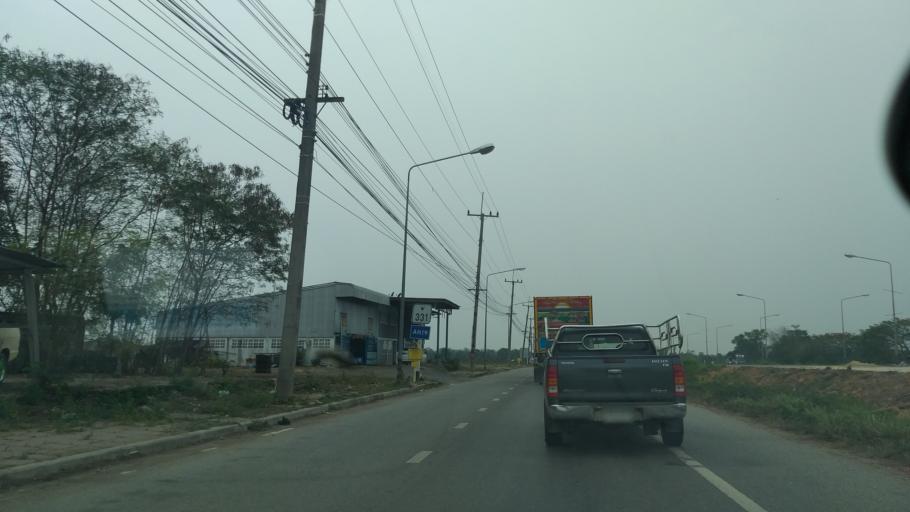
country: TH
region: Chon Buri
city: Ko Chan
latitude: 13.4865
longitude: 101.2776
